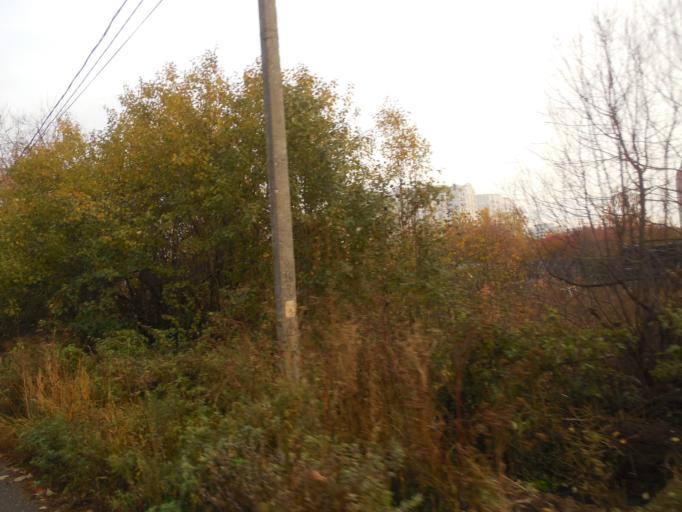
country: RU
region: Moskovskaya
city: Shcherbinka
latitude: 55.5066
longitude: 37.5832
